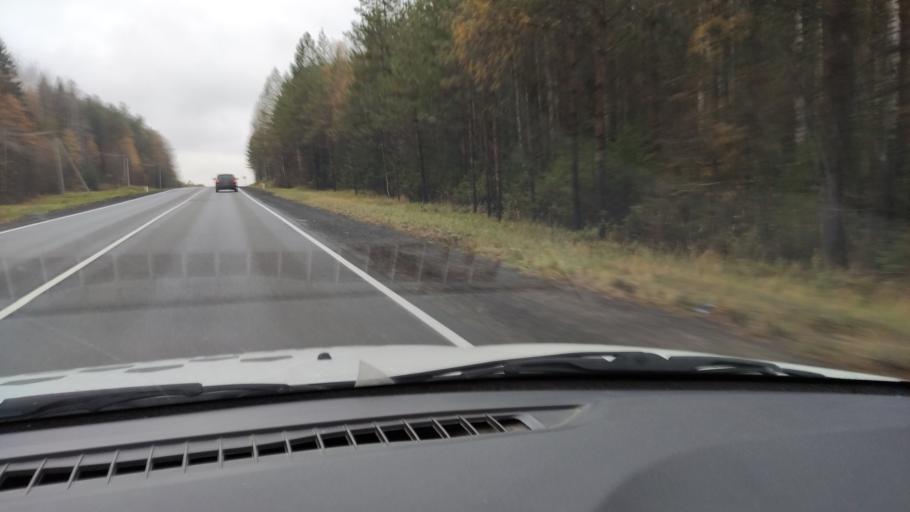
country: RU
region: Kirov
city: Belaya Kholunitsa
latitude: 58.9058
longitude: 51.0266
